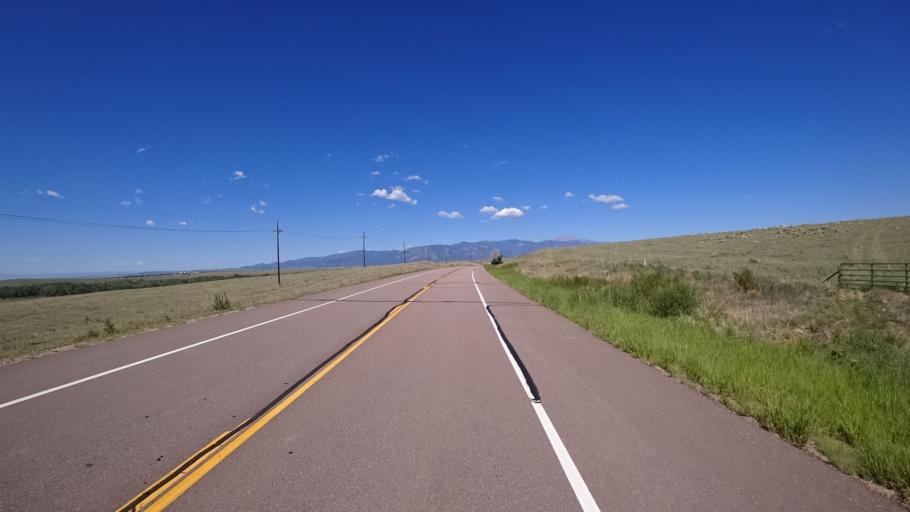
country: US
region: Colorado
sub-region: El Paso County
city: Security-Widefield
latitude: 38.7614
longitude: -104.6463
